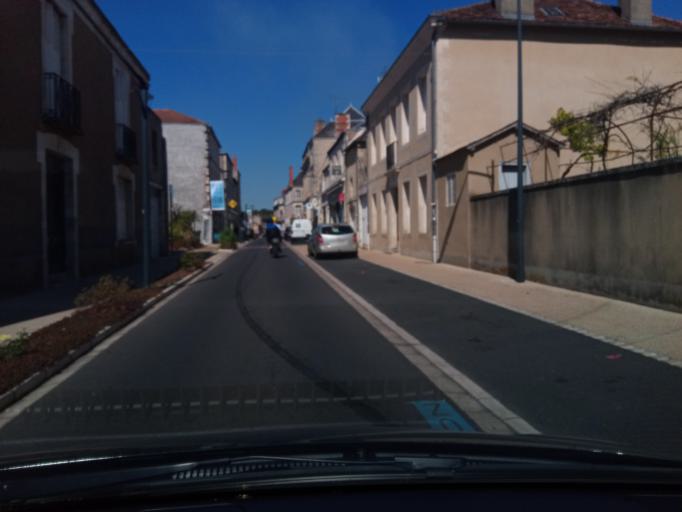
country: FR
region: Poitou-Charentes
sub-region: Departement de la Vienne
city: Montmorillon
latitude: 46.4255
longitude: 0.8699
